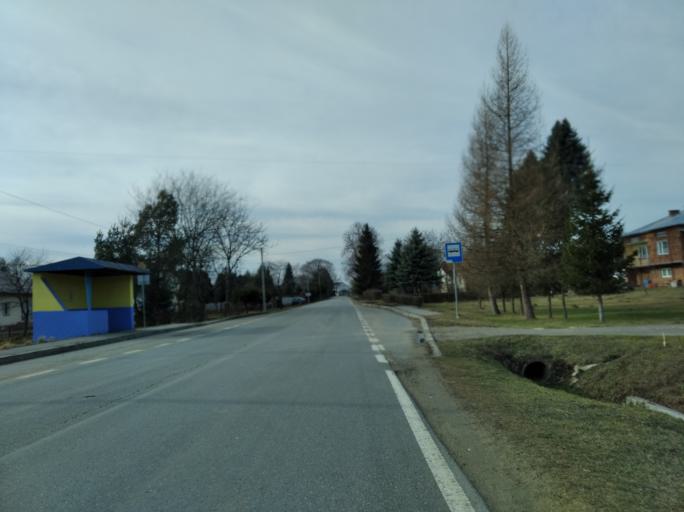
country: PL
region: Subcarpathian Voivodeship
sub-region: Powiat brzozowski
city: Turze Pole
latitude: 49.6613
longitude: 22.0076
